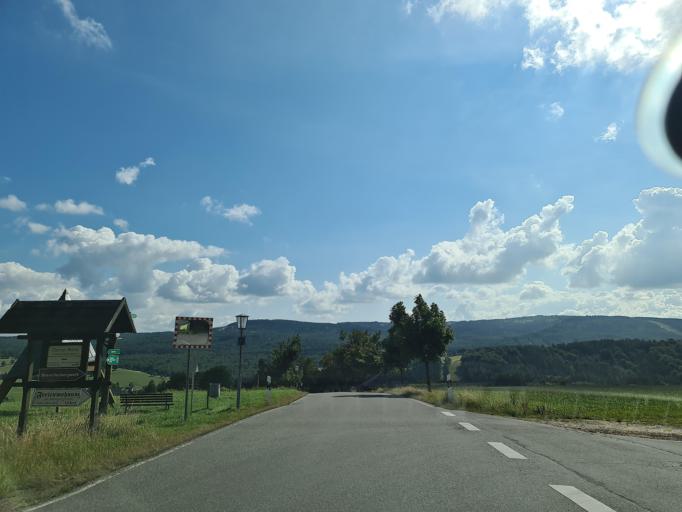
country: DE
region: Saxony
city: Deutschneudorf
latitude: 50.6104
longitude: 13.4624
